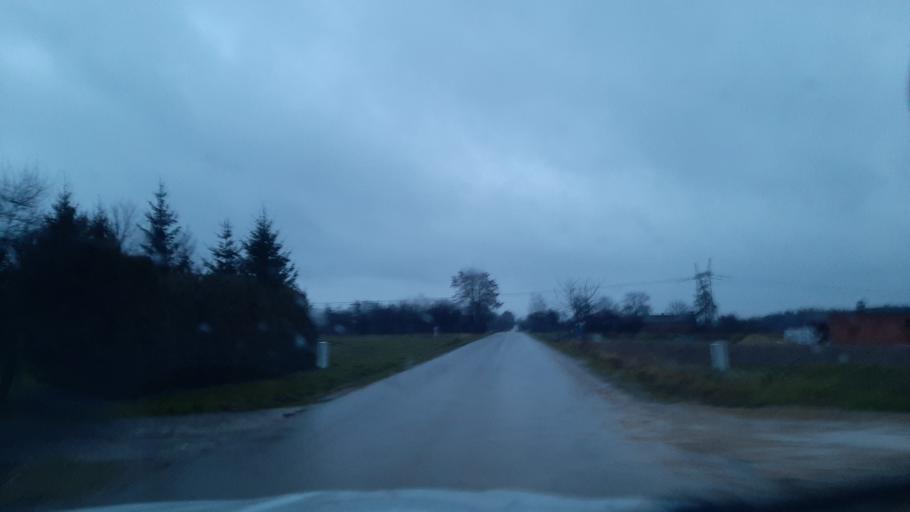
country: PL
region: Lublin Voivodeship
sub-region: Powiat lubelski
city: Jastkow
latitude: 51.3559
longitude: 22.4191
